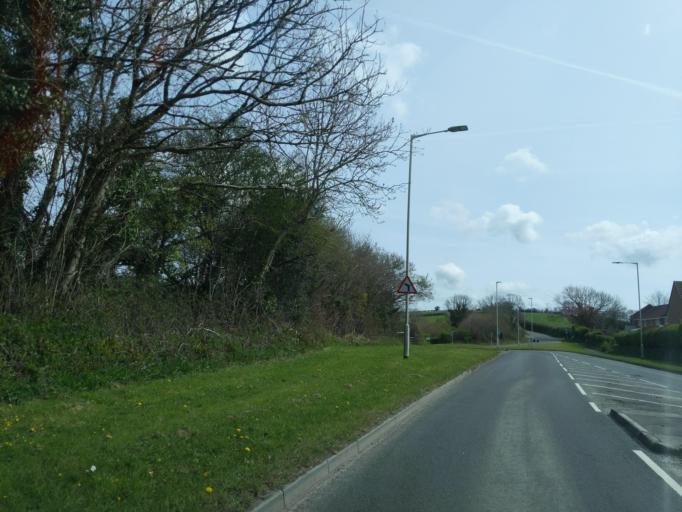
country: GB
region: England
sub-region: Devon
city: Plympton
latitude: 50.3974
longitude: -4.0330
